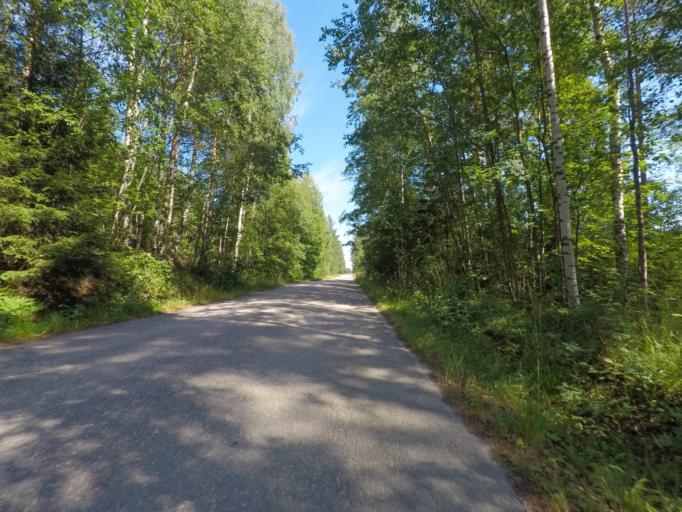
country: FI
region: Southern Savonia
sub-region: Mikkeli
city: Puumala
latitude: 61.4056
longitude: 28.0526
